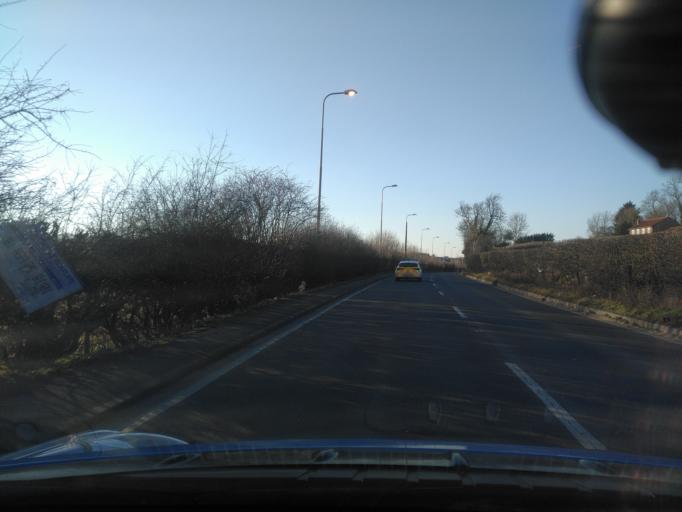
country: GB
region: England
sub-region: Hertfordshire
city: Flamstead
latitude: 51.8255
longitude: -0.4378
